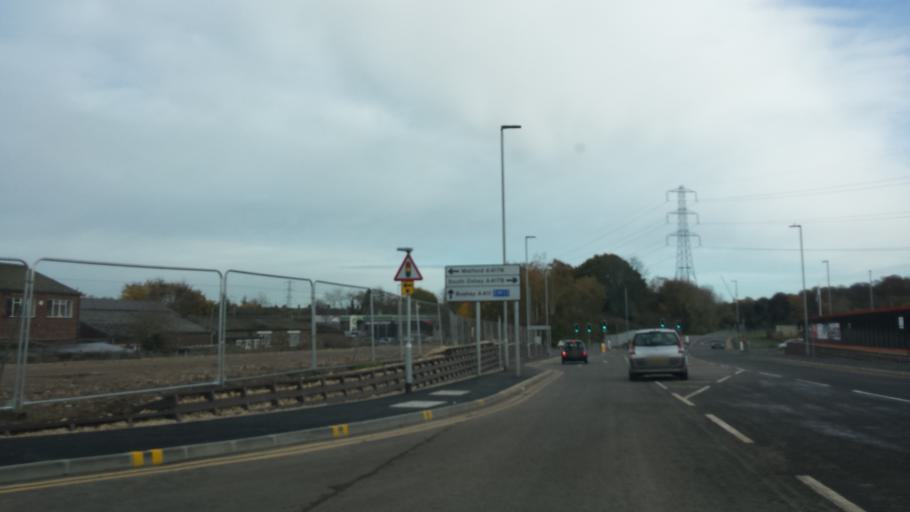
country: GB
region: England
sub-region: Hertfordshire
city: Watford
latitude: 51.6471
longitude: -0.3967
